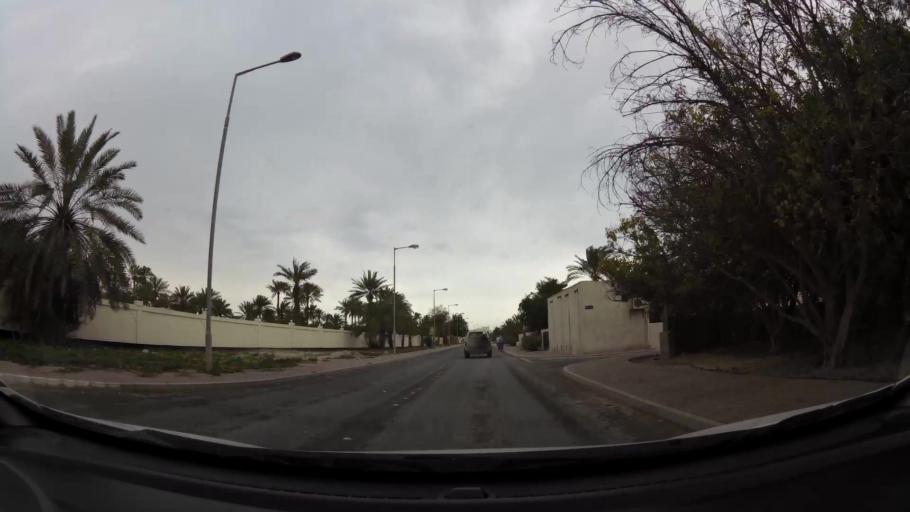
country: BH
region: Central Governorate
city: Madinat Hamad
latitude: 26.1596
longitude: 50.4516
